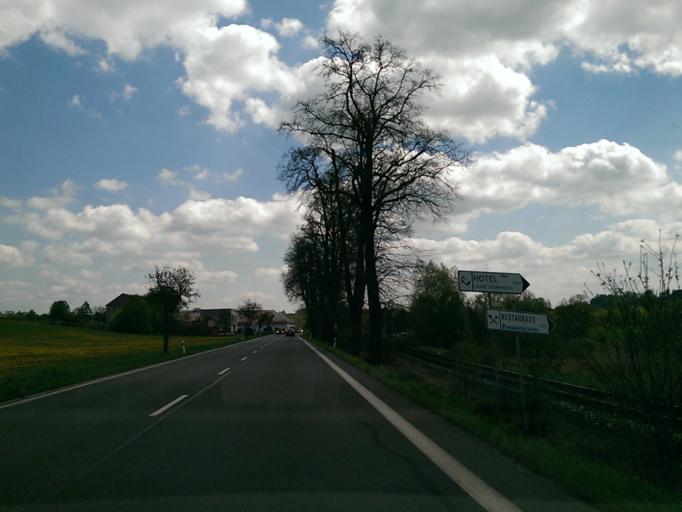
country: CZ
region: Liberecky
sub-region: Okres Semily
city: Turnov
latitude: 50.5629
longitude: 15.1945
